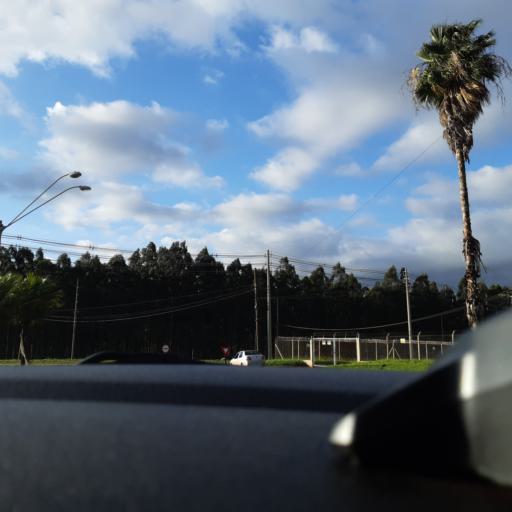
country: BR
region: Sao Paulo
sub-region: Ourinhos
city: Ourinhos
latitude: -22.9966
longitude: -49.8526
